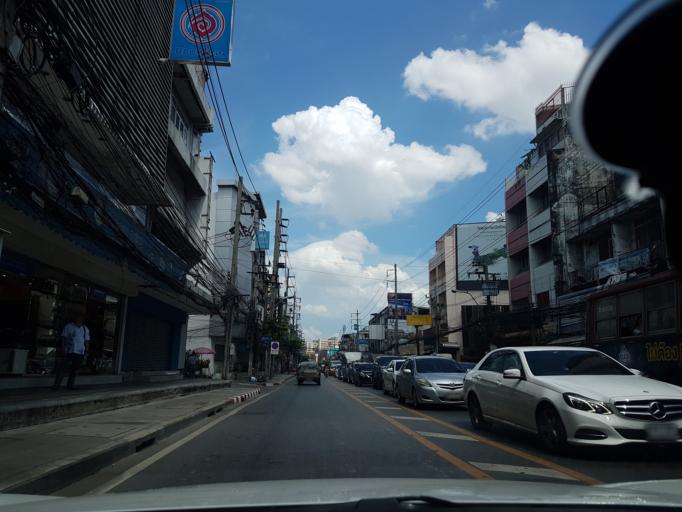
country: TH
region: Bangkok
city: Phra Khanong
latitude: 13.7138
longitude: 100.5945
